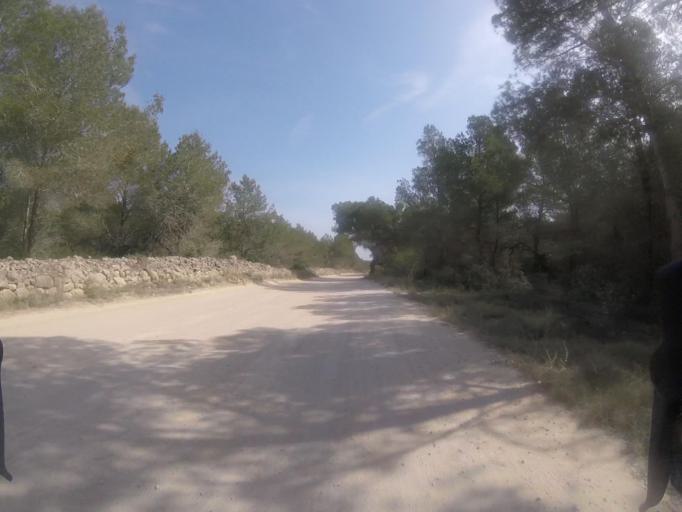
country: ES
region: Valencia
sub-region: Provincia de Castello
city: Alcoceber
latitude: 40.2691
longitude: 0.3024
